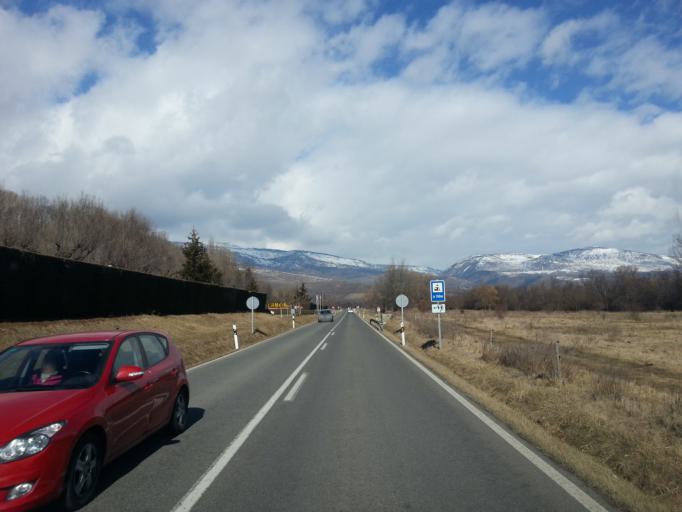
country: FR
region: Languedoc-Roussillon
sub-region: Departement des Pyrenees-Orientales
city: la Guingueta d'Ix
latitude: 42.4400
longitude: 1.9418
